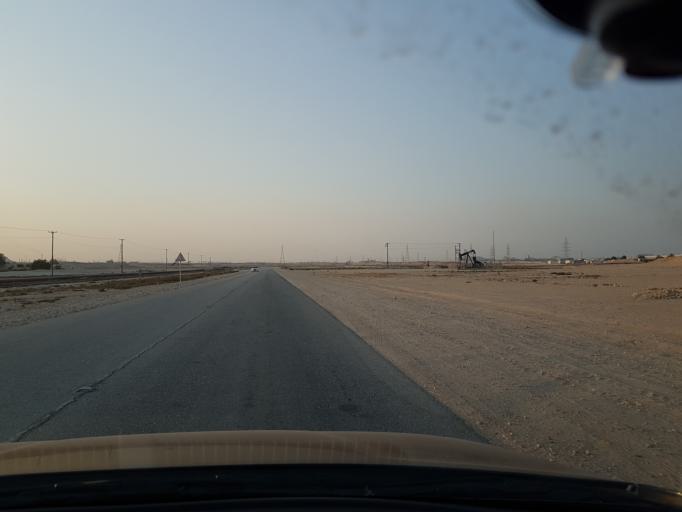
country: BH
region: Central Governorate
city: Dar Kulayb
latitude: 26.0080
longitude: 50.5812
